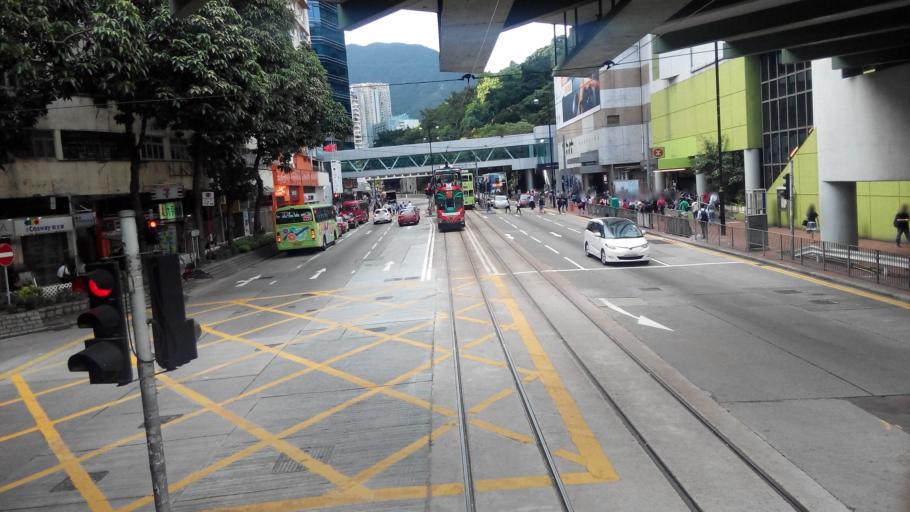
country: HK
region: Wanchai
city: Wan Chai
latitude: 22.2882
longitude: 114.2099
